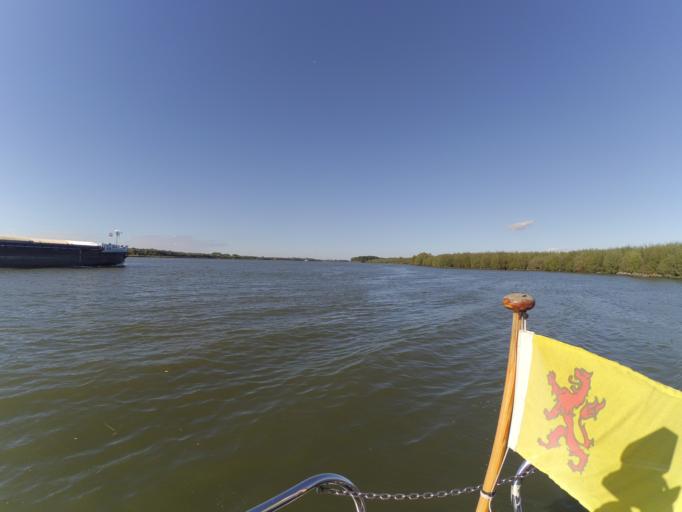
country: NL
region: South Holland
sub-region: Gemeente Binnenmaas
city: Heinenoord
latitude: 51.8369
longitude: 4.4900
